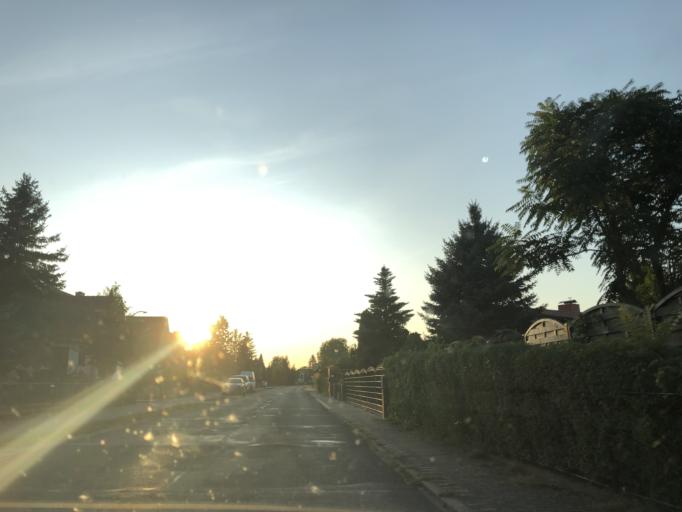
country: DE
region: Brandenburg
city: Mullrose
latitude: 52.2526
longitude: 14.4308
